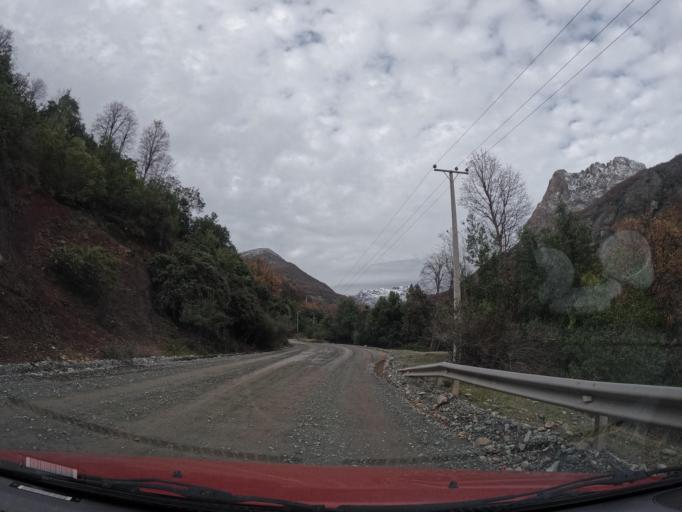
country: CL
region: Maule
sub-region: Provincia de Linares
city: Colbun
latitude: -35.8561
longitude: -71.2058
